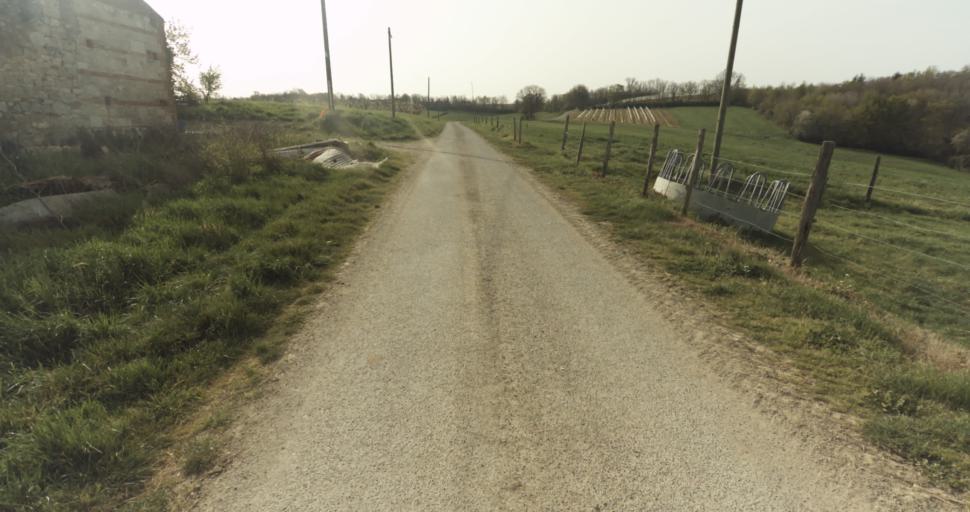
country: FR
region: Midi-Pyrenees
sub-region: Departement du Tarn-et-Garonne
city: Moissac
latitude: 44.1618
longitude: 1.0242
